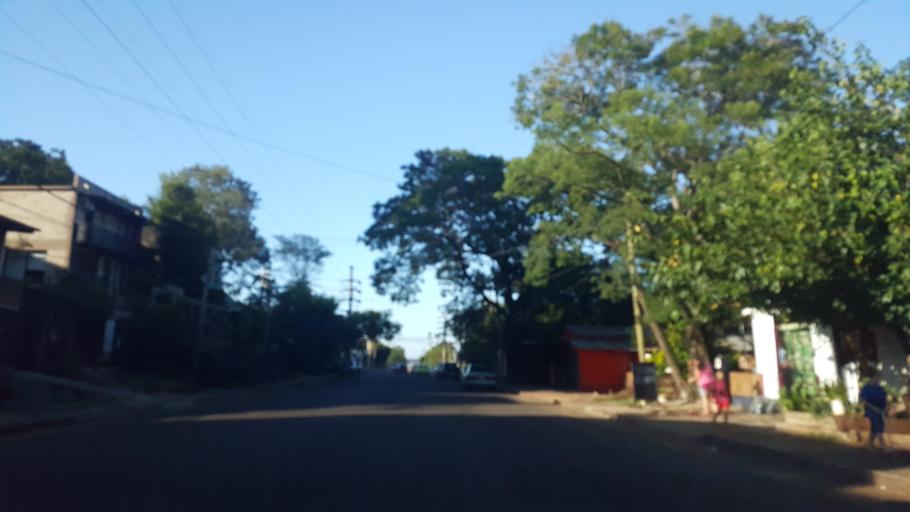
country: AR
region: Misiones
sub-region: Departamento de Capital
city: Posadas
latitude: -27.3613
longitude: -55.9043
